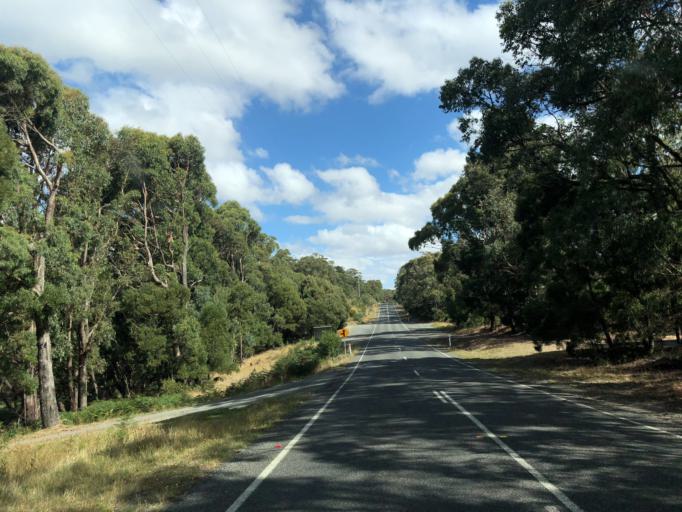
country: AU
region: Victoria
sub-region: Moorabool
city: Bacchus Marsh
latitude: -37.5149
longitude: 144.3118
